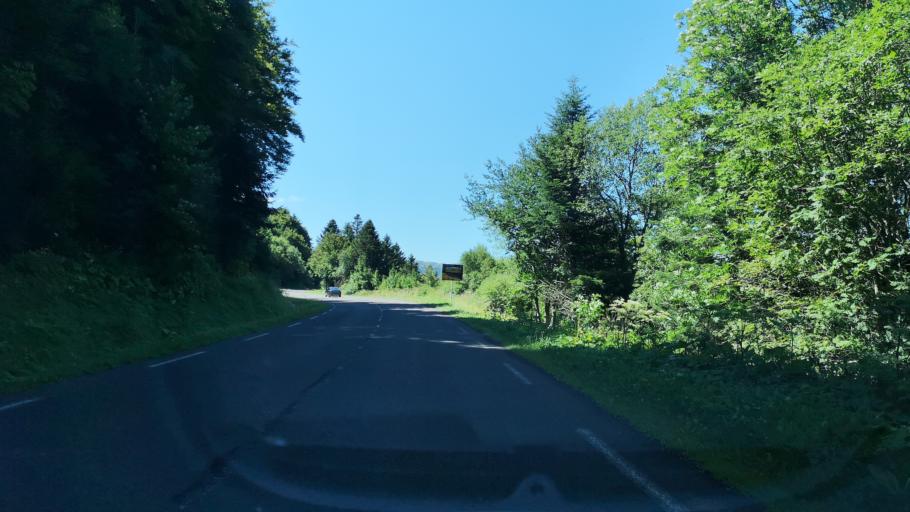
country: FR
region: Auvergne
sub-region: Departement du Puy-de-Dome
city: Mont-Dore
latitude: 45.5946
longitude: 2.8273
